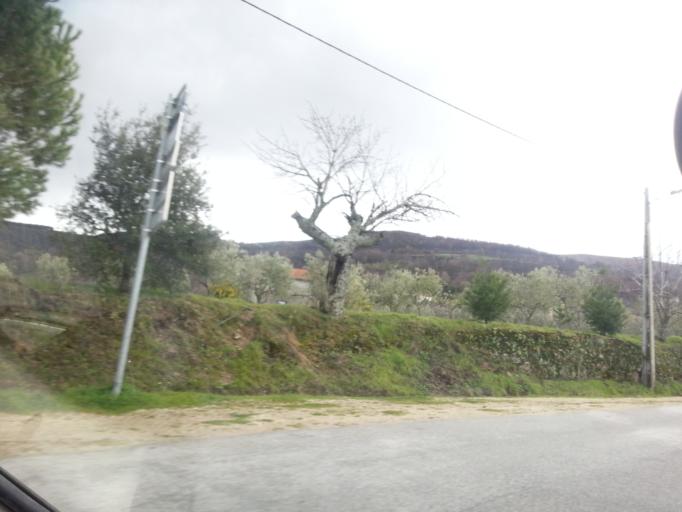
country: PT
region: Guarda
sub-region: Celorico da Beira
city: Celorico da Beira
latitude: 40.5488
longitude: -7.4556
